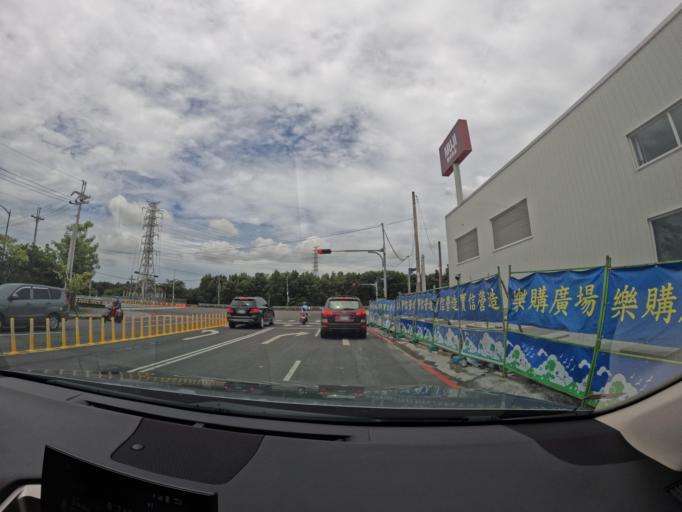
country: TW
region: Kaohsiung
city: Kaohsiung
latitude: 22.7790
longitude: 120.2997
